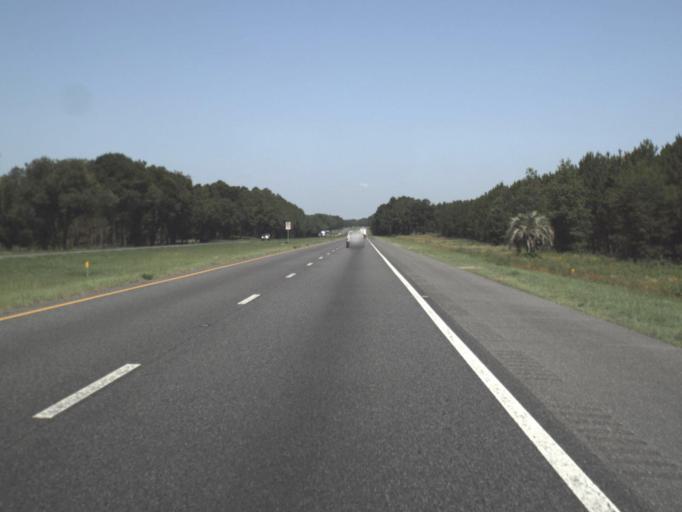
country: US
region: Florida
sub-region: Suwannee County
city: Wellborn
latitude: 30.2887
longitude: -82.8572
